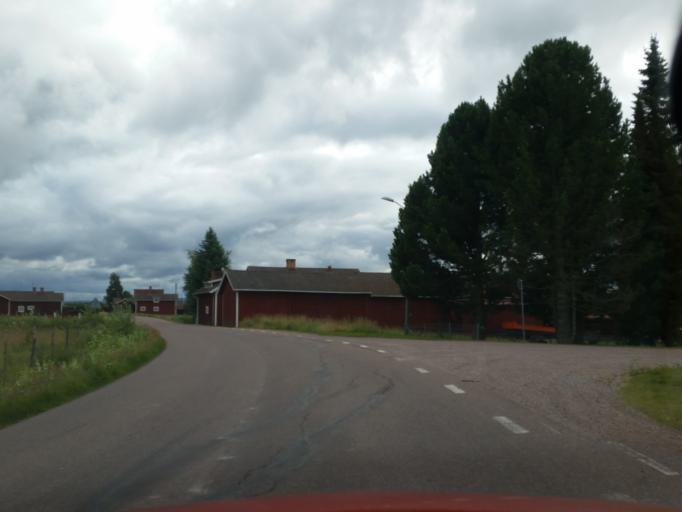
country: SE
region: Dalarna
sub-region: Leksand Municipality
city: Smedby
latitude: 60.7154
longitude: 15.0473
